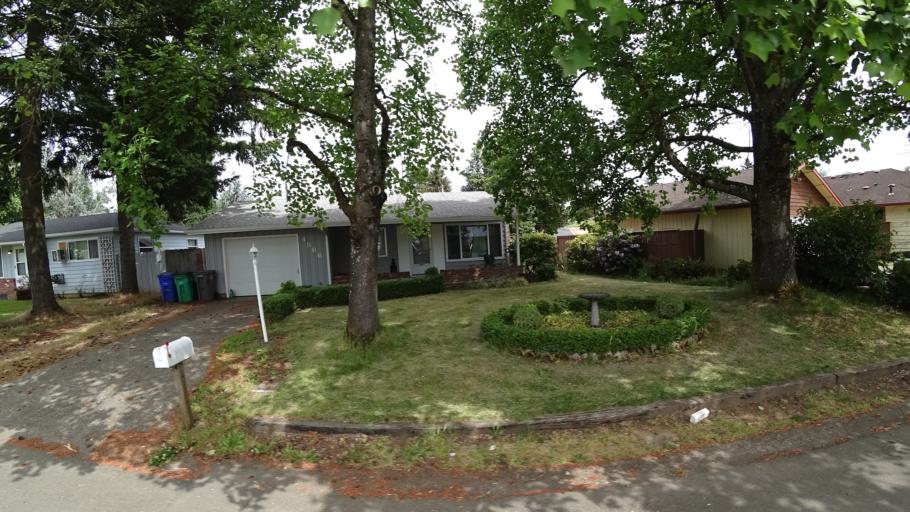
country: US
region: Oregon
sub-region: Multnomah County
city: Lents
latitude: 45.4886
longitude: -122.5467
